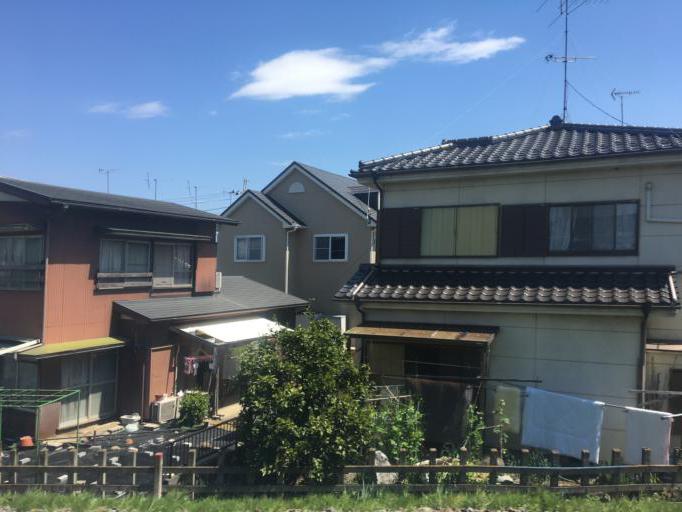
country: JP
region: Saitama
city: Kawagoe
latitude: 35.9190
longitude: 139.4715
